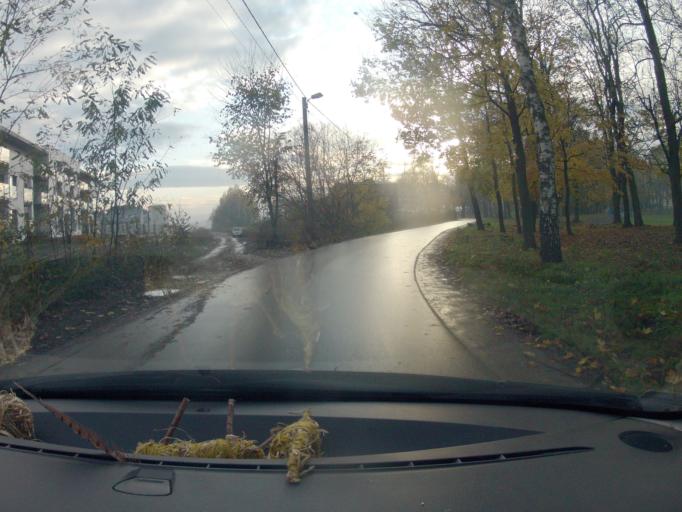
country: PL
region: Lesser Poland Voivodeship
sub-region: Krakow
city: Sidzina
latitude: 50.0024
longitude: 19.8888
